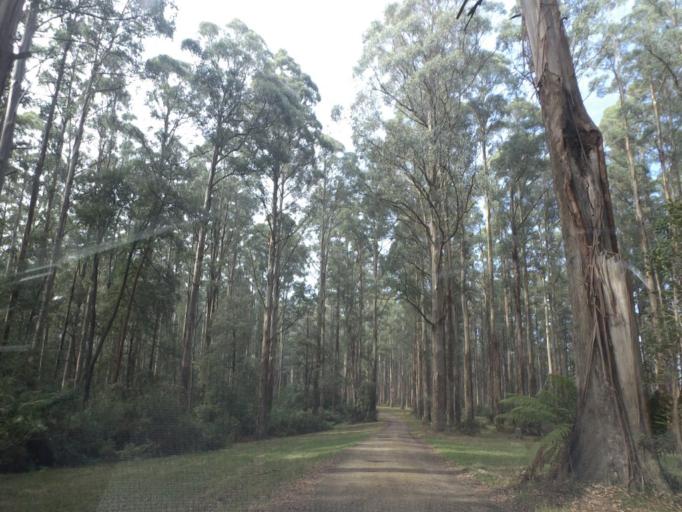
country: AU
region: Victoria
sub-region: Yarra Ranges
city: Healesville
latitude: -37.5805
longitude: 145.5522
